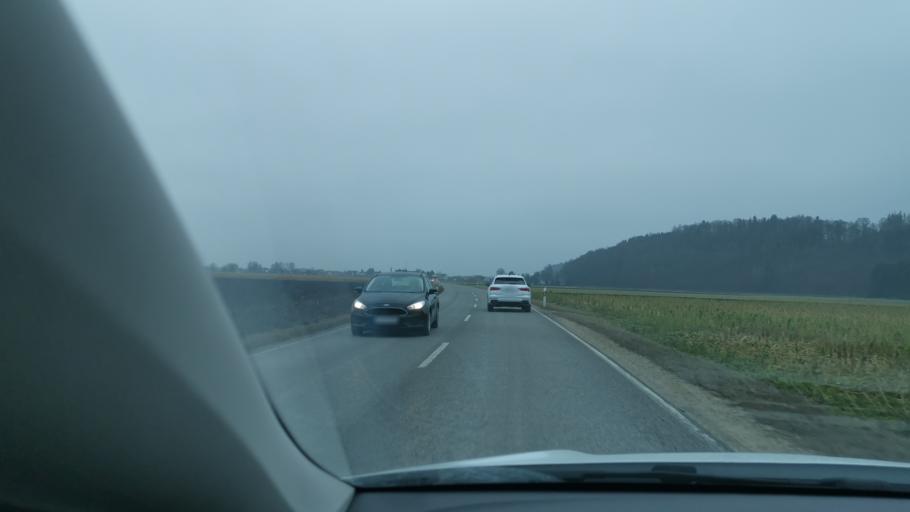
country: DE
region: Bavaria
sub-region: Swabia
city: Todtenweis
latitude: 48.5057
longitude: 10.9203
